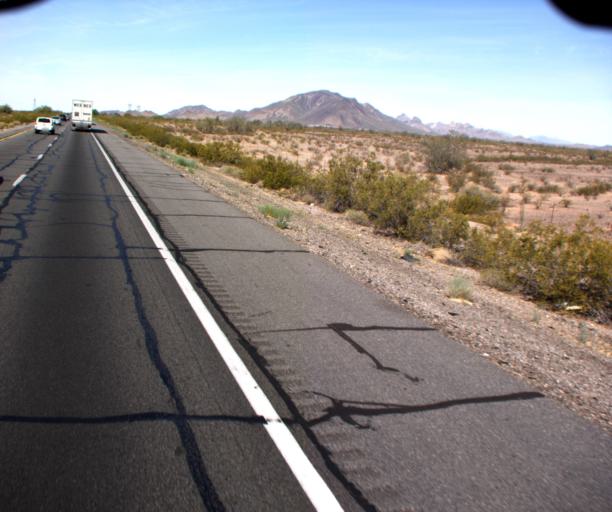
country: US
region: Arizona
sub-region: Maricopa County
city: Buckeye
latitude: 33.5108
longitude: -113.0103
